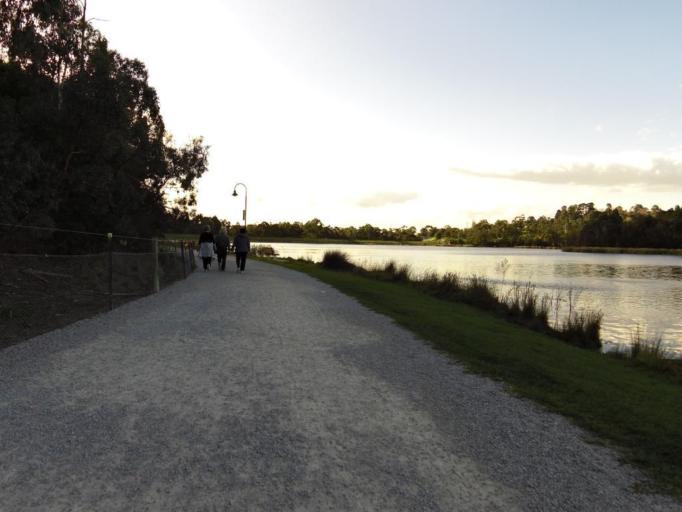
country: AU
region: Victoria
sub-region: Yarra Ranges
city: Lilydale
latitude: -37.7668
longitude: 145.3515
